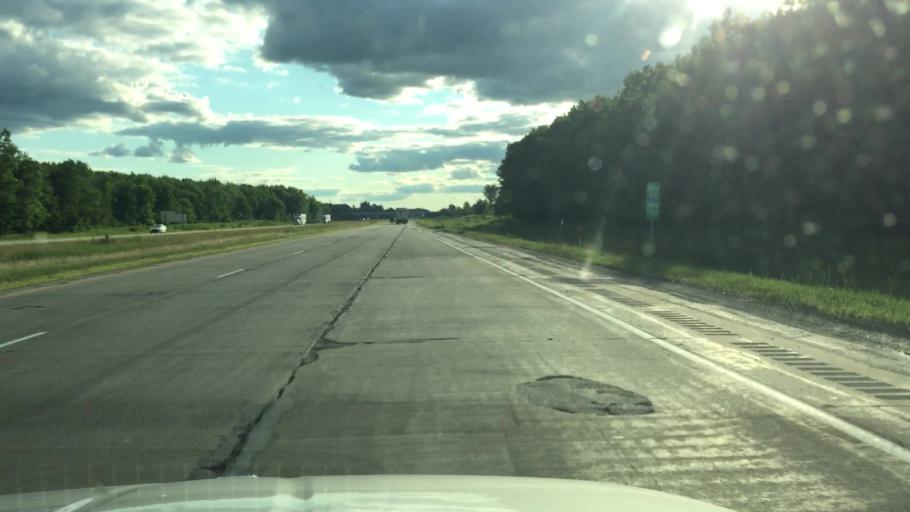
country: US
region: Michigan
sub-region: Macomb County
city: Memphis
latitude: 42.9797
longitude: -82.7724
